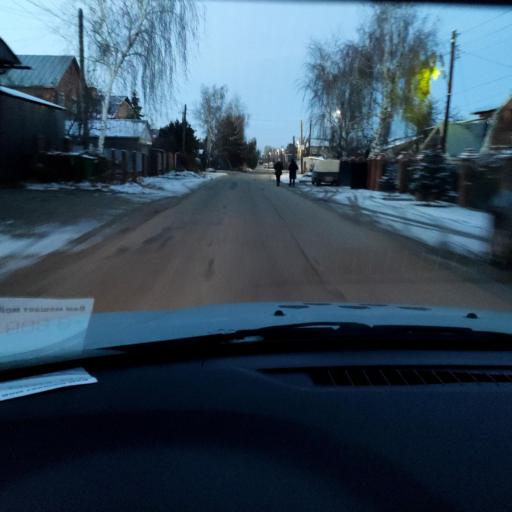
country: RU
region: Samara
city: Tol'yatti
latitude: 53.5611
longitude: 49.3889
